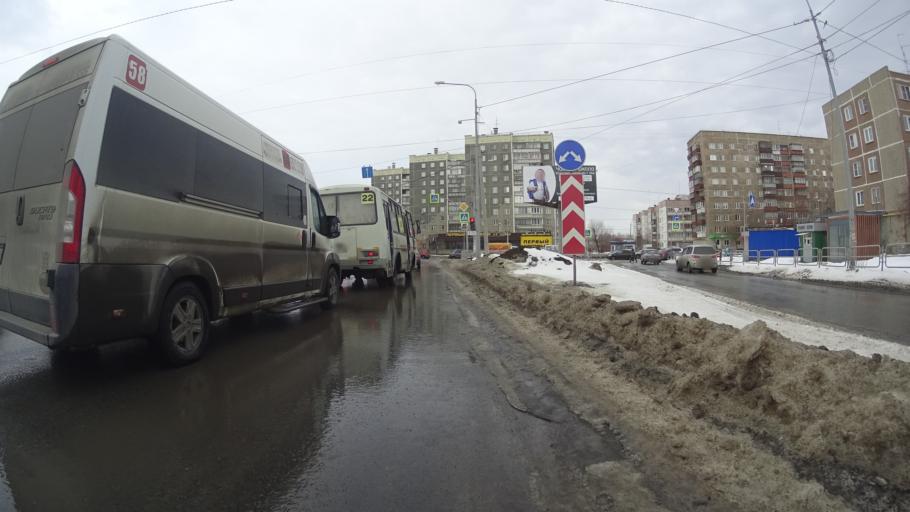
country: RU
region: Chelyabinsk
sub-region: Gorod Chelyabinsk
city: Chelyabinsk
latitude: 55.1979
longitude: 61.3327
